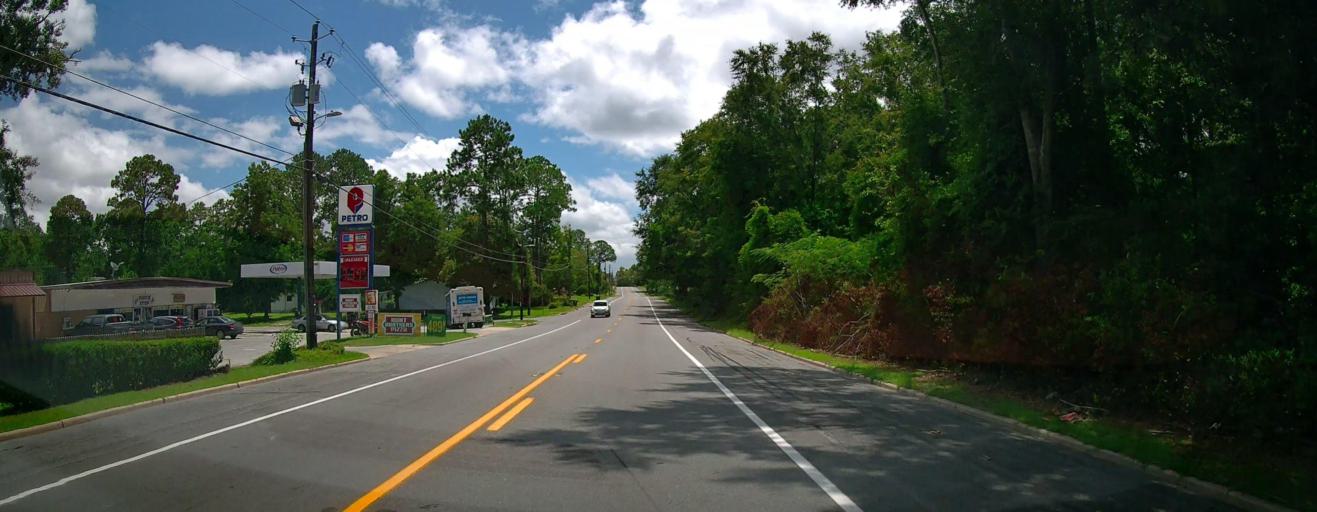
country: US
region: Georgia
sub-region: Turner County
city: Ashburn
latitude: 31.7151
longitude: -83.6546
